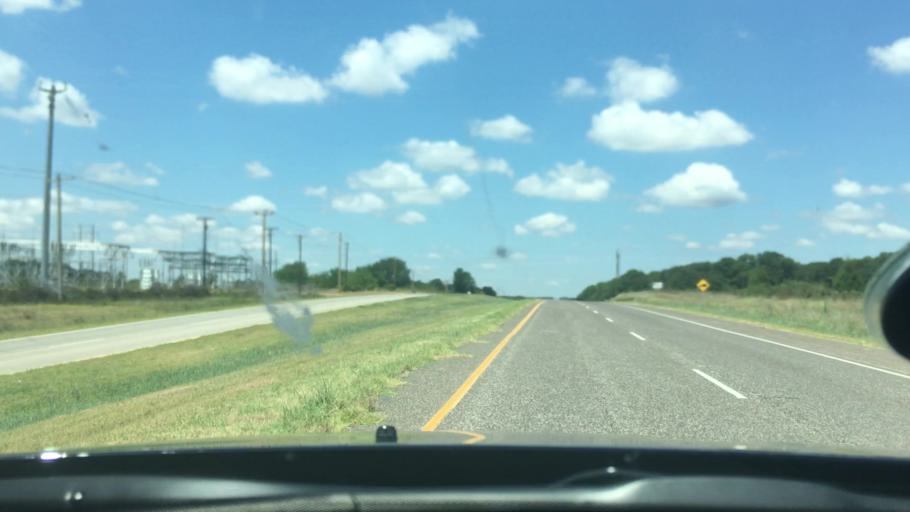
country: US
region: Oklahoma
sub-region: Carter County
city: Lone Grove
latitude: 34.1730
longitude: -97.3306
